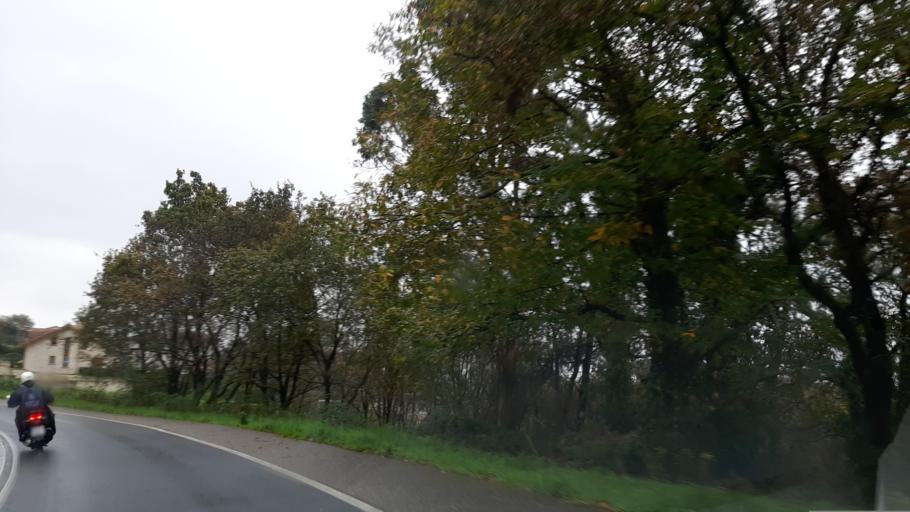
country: ES
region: Galicia
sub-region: Provincia de Pontevedra
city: Nigran
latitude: 42.1715
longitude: -8.8005
